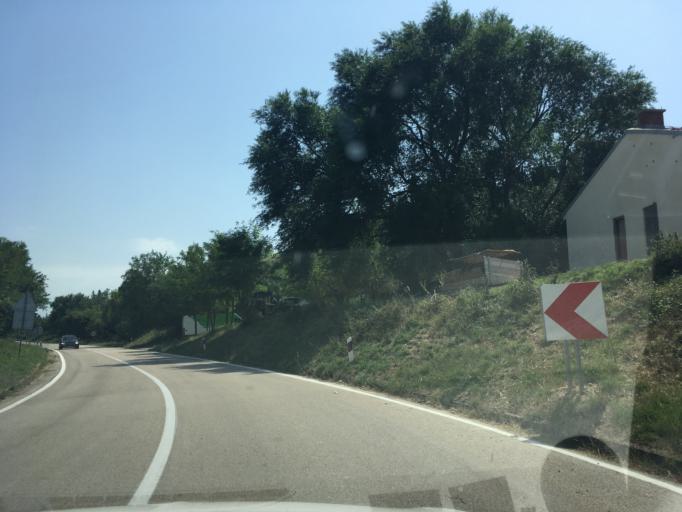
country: HR
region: Sibensko-Kniniska
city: Zaton
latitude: 43.9289
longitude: 15.8125
